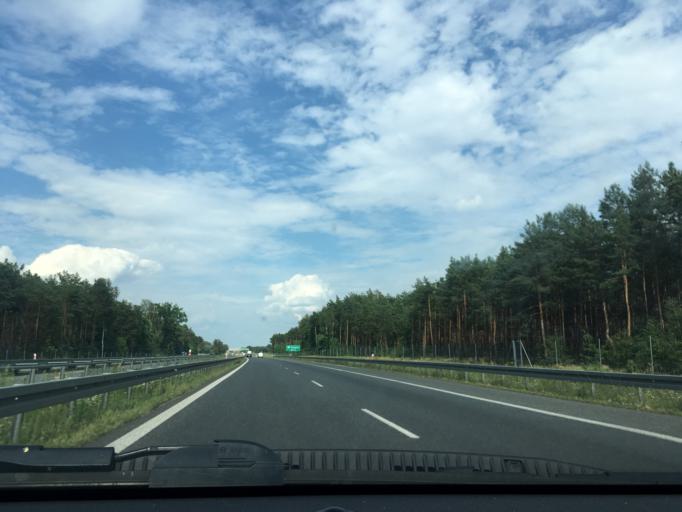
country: PL
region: Masovian Voivodeship
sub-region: Powiat wolominski
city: Dabrowka
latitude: 52.4987
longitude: 21.3766
